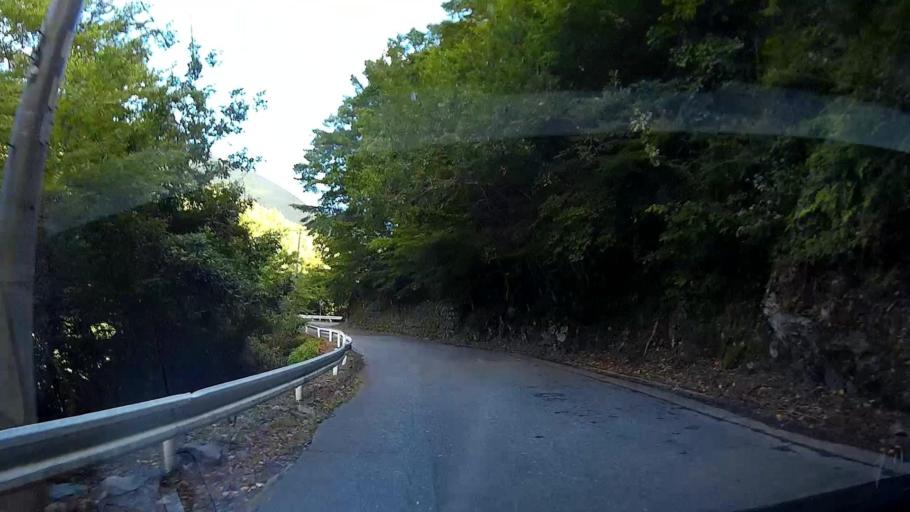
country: JP
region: Shizuoka
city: Shizuoka-shi
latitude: 35.3019
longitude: 138.2164
